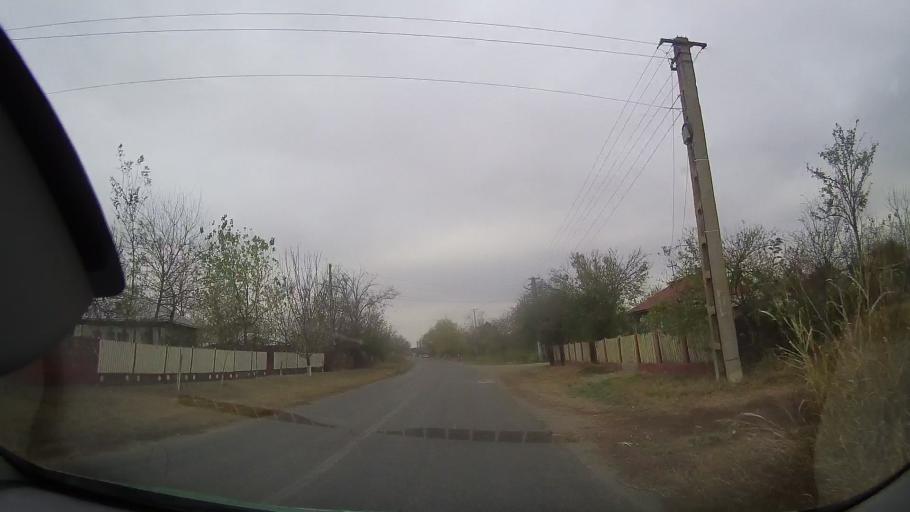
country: RO
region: Buzau
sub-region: Comuna Largu
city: Largu
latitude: 44.9704
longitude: 27.1819
